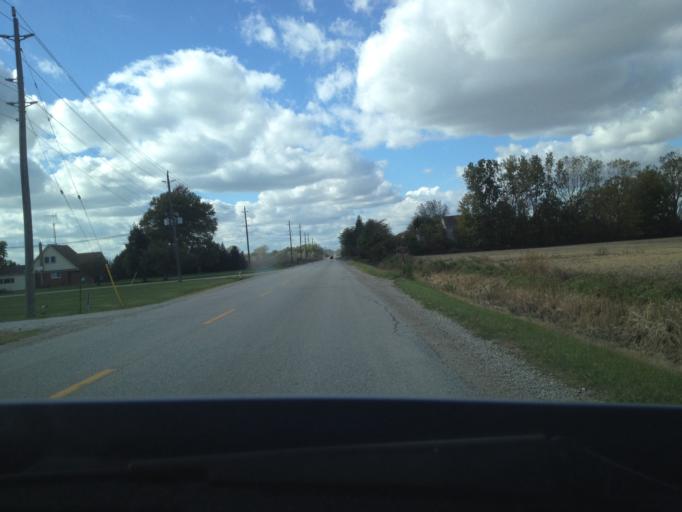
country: CA
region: Ontario
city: Amherstburg
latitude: 42.0327
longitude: -82.5698
